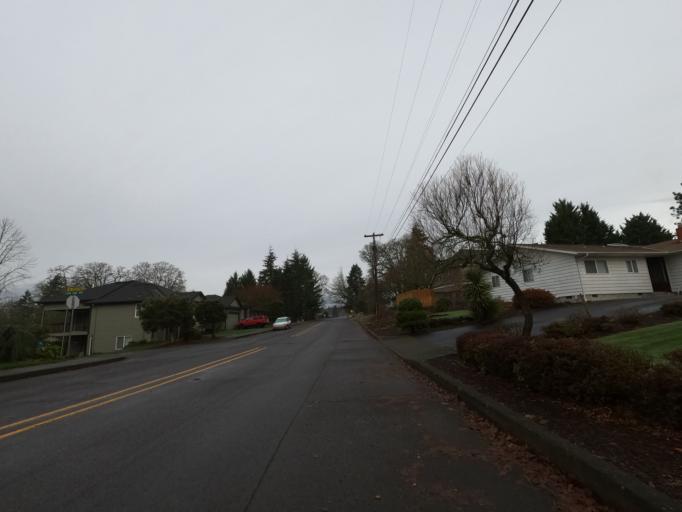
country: US
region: Oregon
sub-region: Clackamas County
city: Jennings Lodge
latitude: 45.3906
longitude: -122.6015
